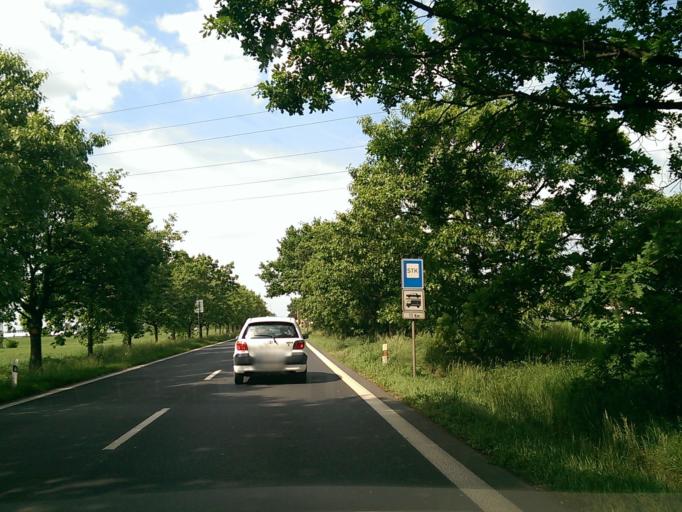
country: CZ
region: Central Bohemia
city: Libis
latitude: 50.2720
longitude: 14.4959
